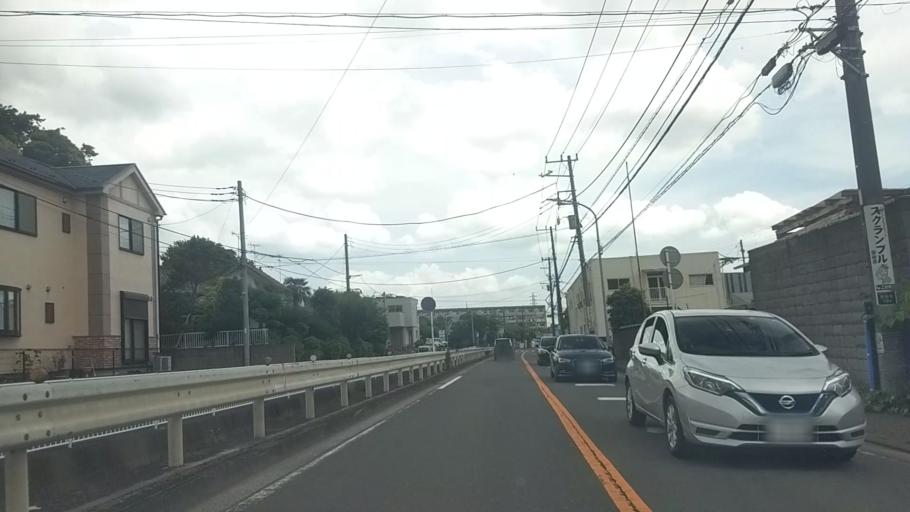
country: JP
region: Kanagawa
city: Fujisawa
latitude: 35.3708
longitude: 139.5220
